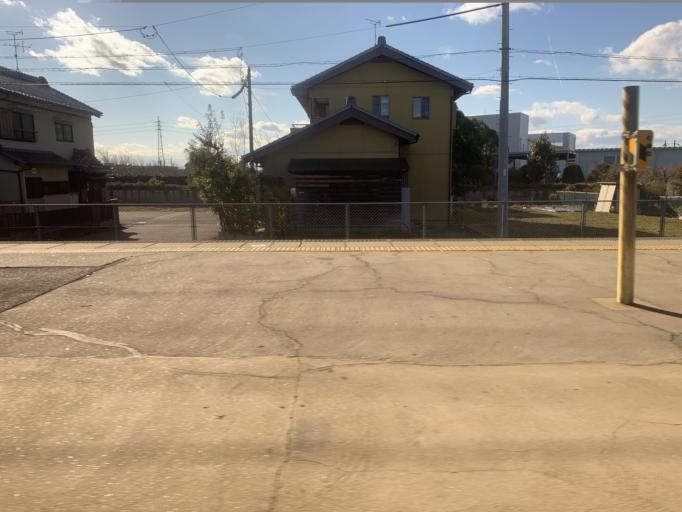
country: JP
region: Aichi
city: Inazawa
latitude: 35.2254
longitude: 136.8345
